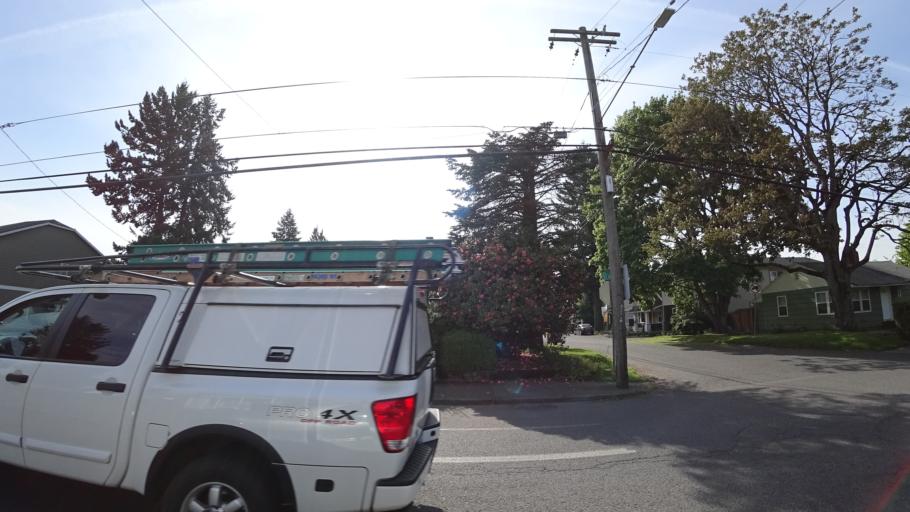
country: US
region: Oregon
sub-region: Clackamas County
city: Milwaukie
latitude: 45.4724
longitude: -122.6160
